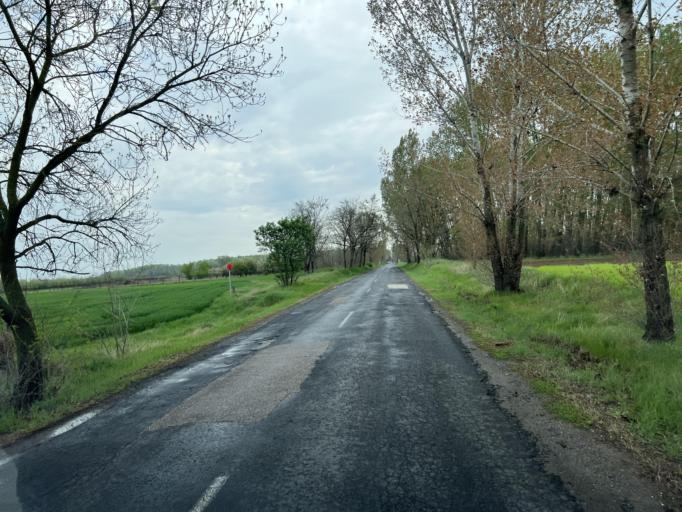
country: HU
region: Pest
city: Danszentmiklos
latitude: 47.2121
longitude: 19.5696
